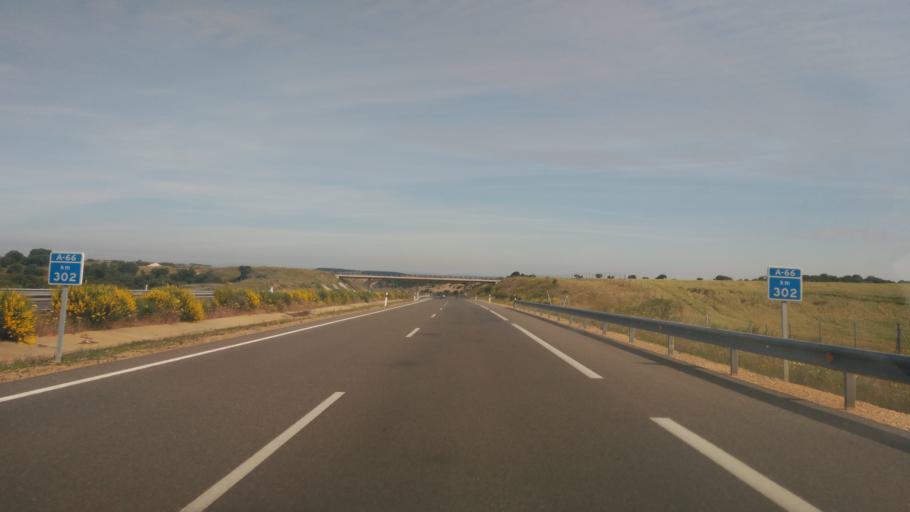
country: ES
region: Castille and Leon
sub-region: Provincia de Zamora
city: Santa Clara de Avedillo
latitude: 41.3050
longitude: -5.7075
